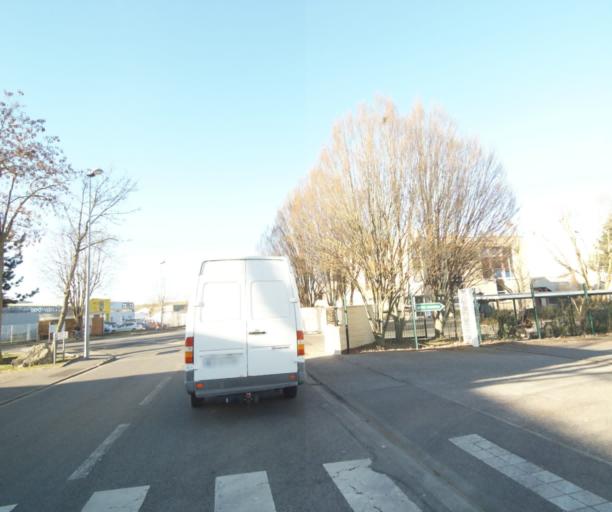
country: FR
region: Lorraine
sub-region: Departement de Meurthe-et-Moselle
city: Pulnoy
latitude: 48.7070
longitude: 6.2529
